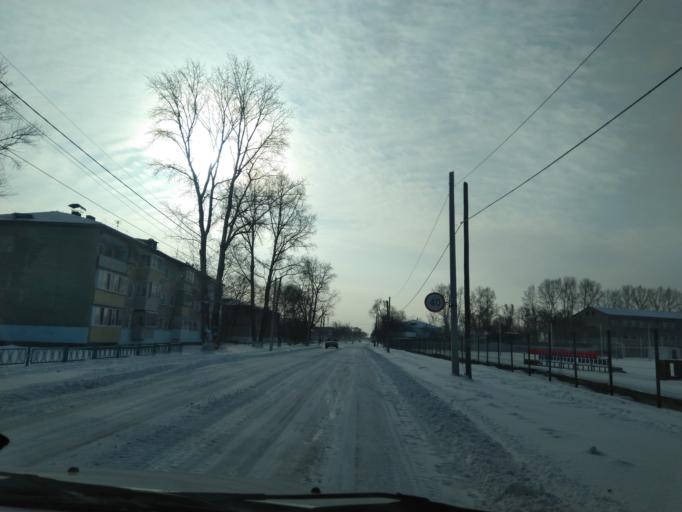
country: RU
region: Amur
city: Poyarkovo
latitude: 49.6247
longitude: 128.6507
